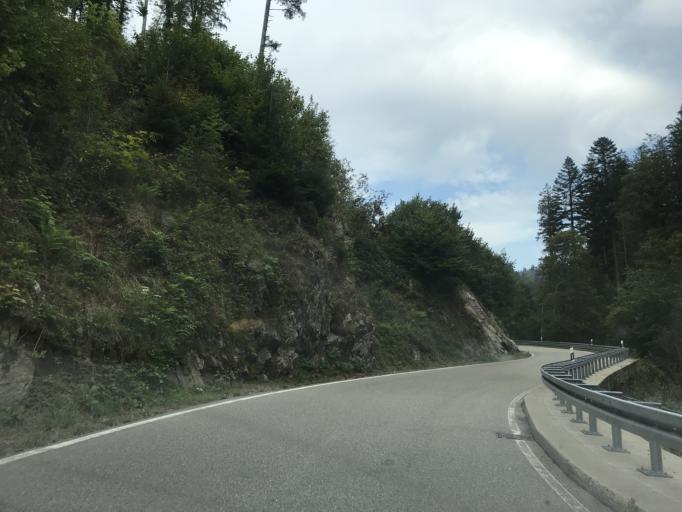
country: DE
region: Baden-Wuerttemberg
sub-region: Freiburg Region
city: Herrischried
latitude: 47.6907
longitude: 7.9677
